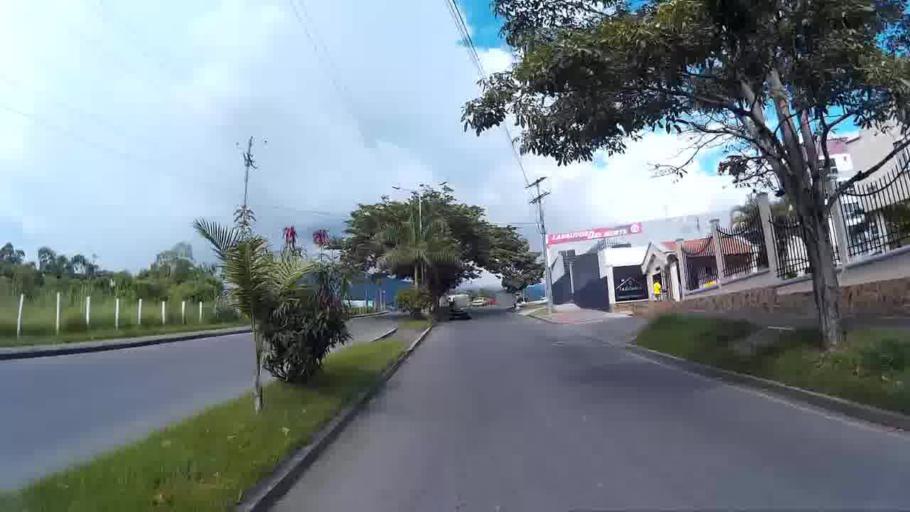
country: CO
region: Quindio
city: Calarca
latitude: 4.5434
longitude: -75.6593
